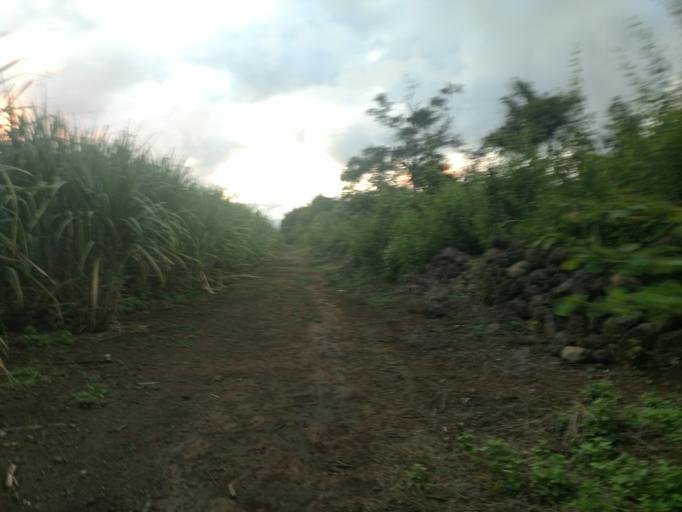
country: MX
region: Nayarit
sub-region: Tepic
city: La Corregidora
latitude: 21.4606
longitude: -104.8063
